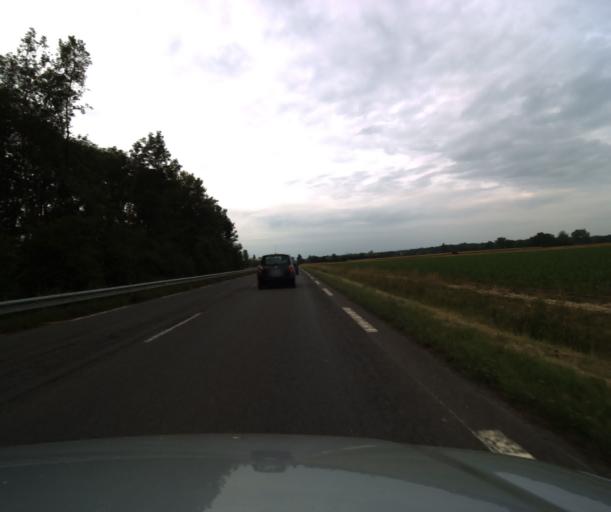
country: FR
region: Midi-Pyrenees
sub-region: Departement des Hautes-Pyrenees
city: Rabastens-de-Bigorre
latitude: 43.3494
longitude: 0.1363
